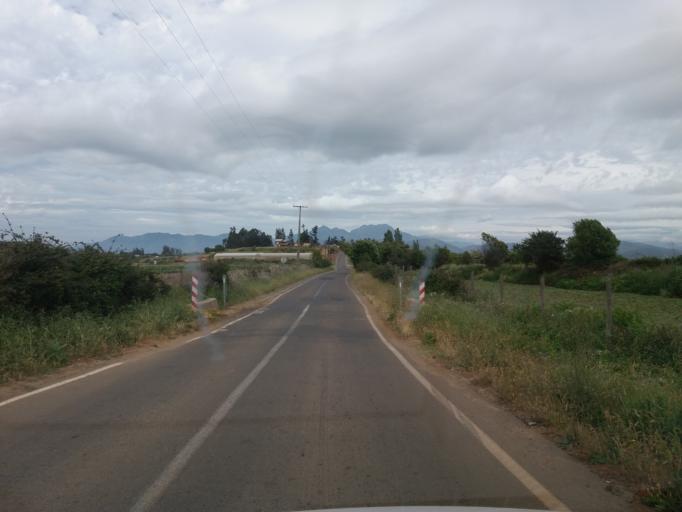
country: CL
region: Valparaiso
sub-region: Provincia de Quillota
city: Quillota
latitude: -32.9164
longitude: -71.3553
